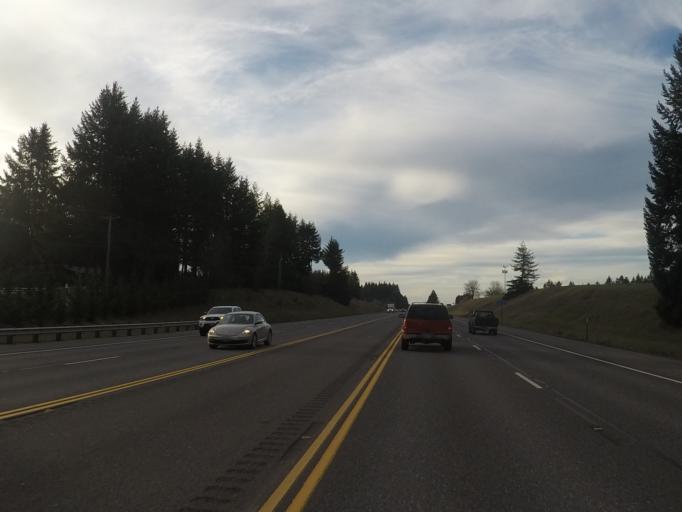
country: US
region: Oregon
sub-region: Clackamas County
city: Sandy
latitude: 45.4140
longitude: -122.3110
